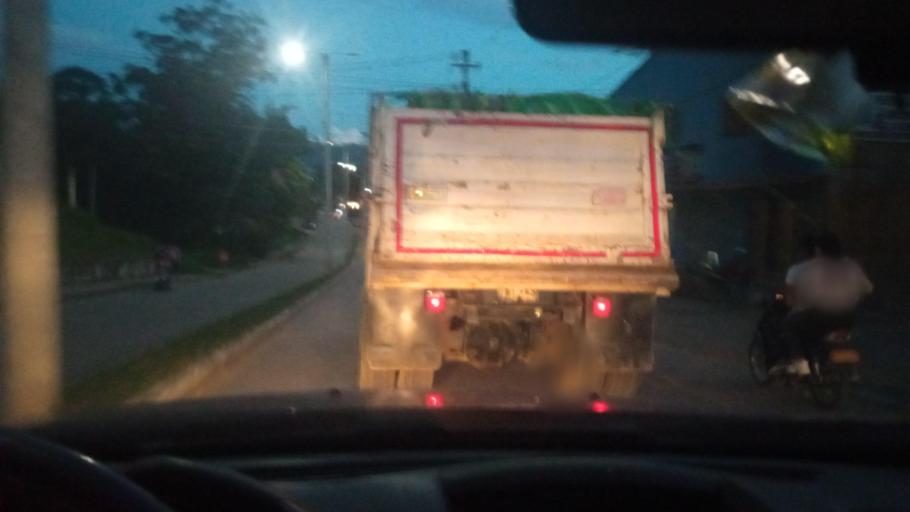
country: CO
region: Huila
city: Pitalito
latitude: 1.8596
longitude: -76.0486
